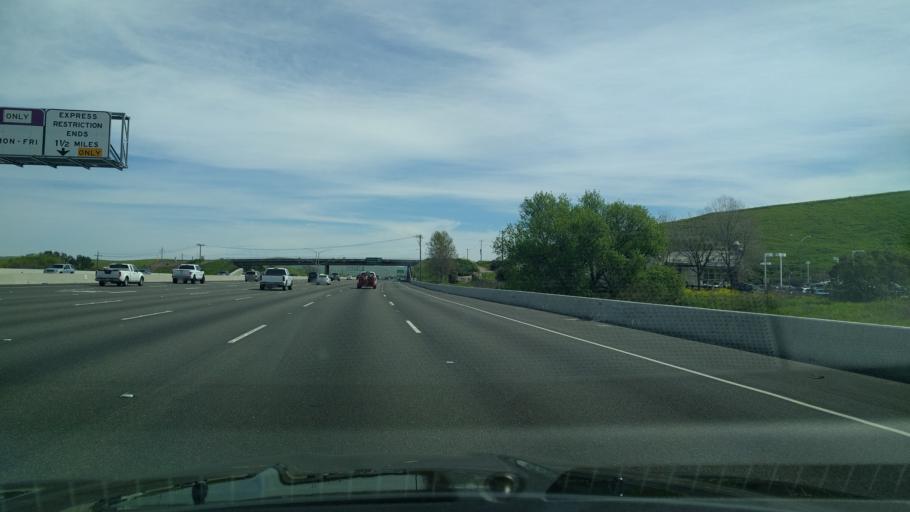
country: US
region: California
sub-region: Alameda County
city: Livermore
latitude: 37.7025
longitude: -121.7587
